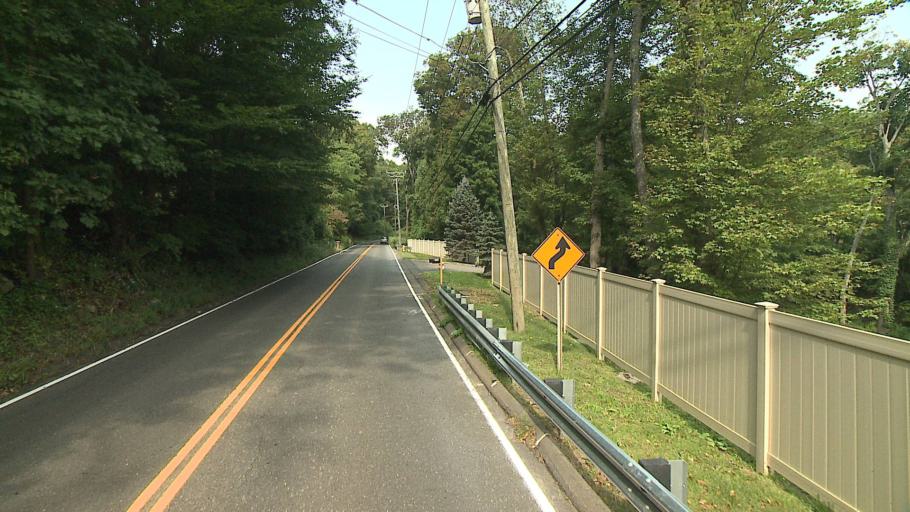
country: US
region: Connecticut
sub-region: Fairfield County
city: Georgetown
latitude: 41.2722
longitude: -73.4639
